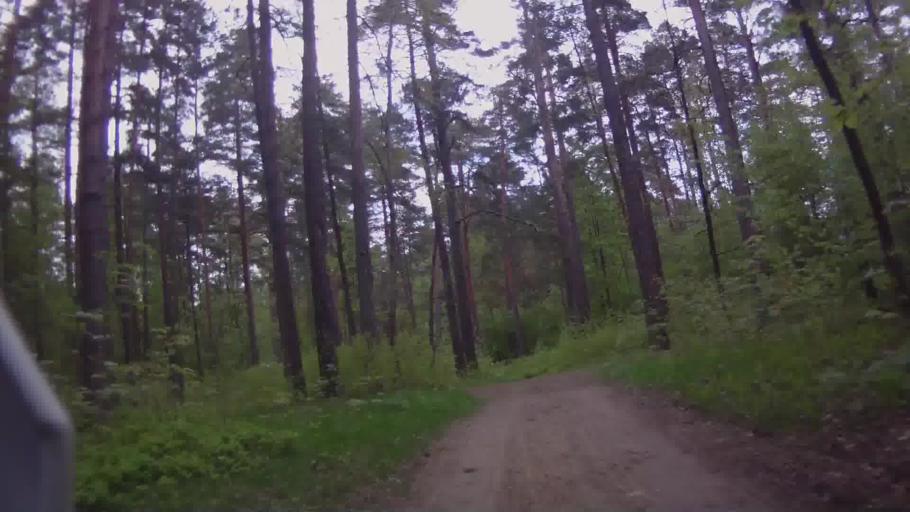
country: LV
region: Stopini
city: Ulbroka
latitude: 56.9599
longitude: 24.2664
